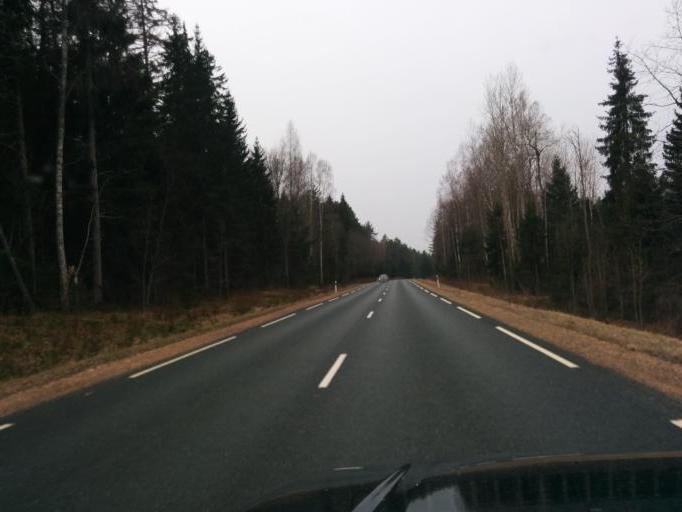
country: LV
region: Ikskile
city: Ikskile
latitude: 56.8009
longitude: 24.5168
